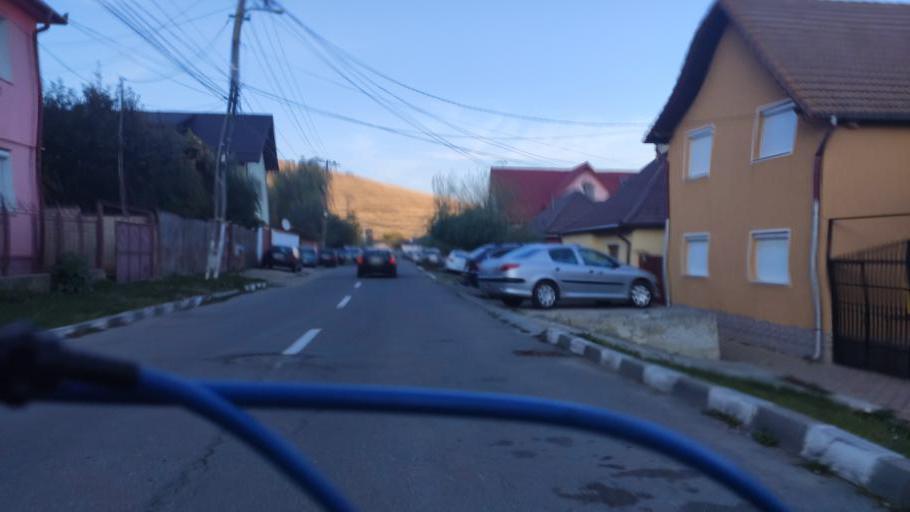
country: RO
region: Brasov
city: Codlea
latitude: 45.7061
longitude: 25.4442
